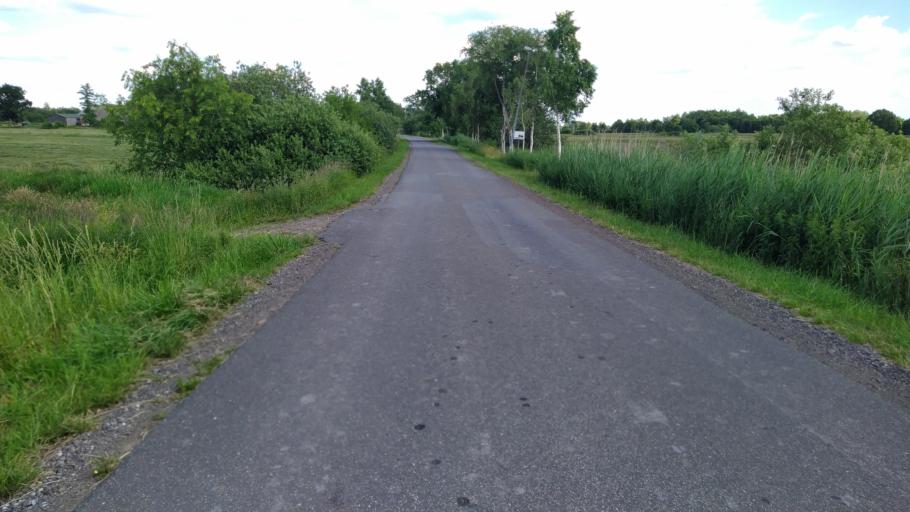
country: DE
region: Lower Saxony
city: Steinau
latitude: 53.6572
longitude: 8.8987
